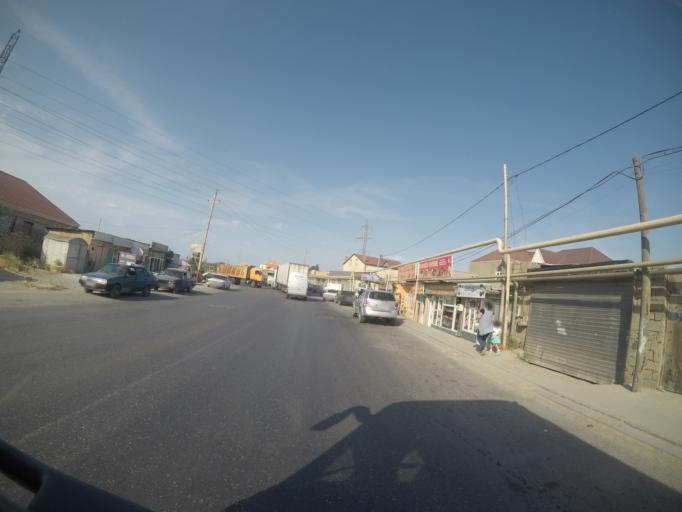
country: AZ
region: Baki
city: Bilajari
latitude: 40.4488
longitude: 49.8030
